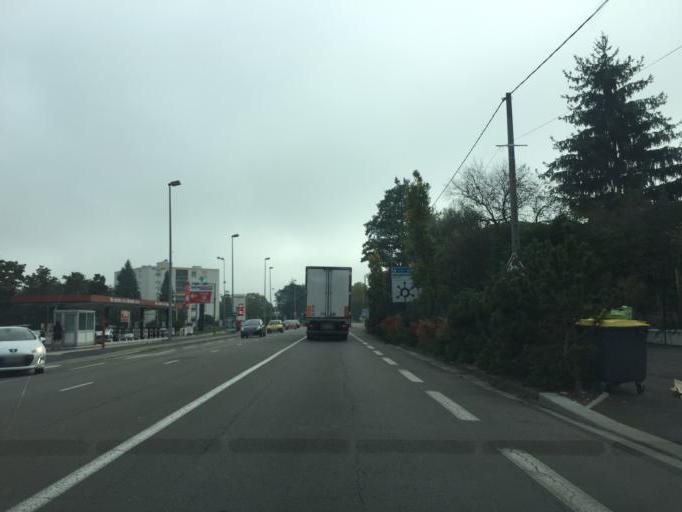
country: FR
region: Rhone-Alpes
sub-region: Departement de l'Ain
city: Bourg-en-Bresse
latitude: 46.1953
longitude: 5.2278
